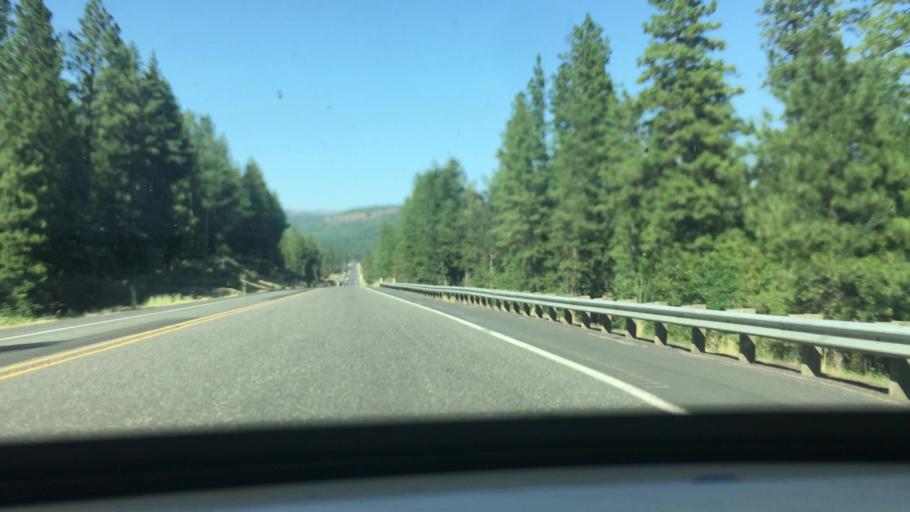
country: US
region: Washington
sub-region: Klickitat County
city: Goldendale
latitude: 45.9362
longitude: -120.6900
